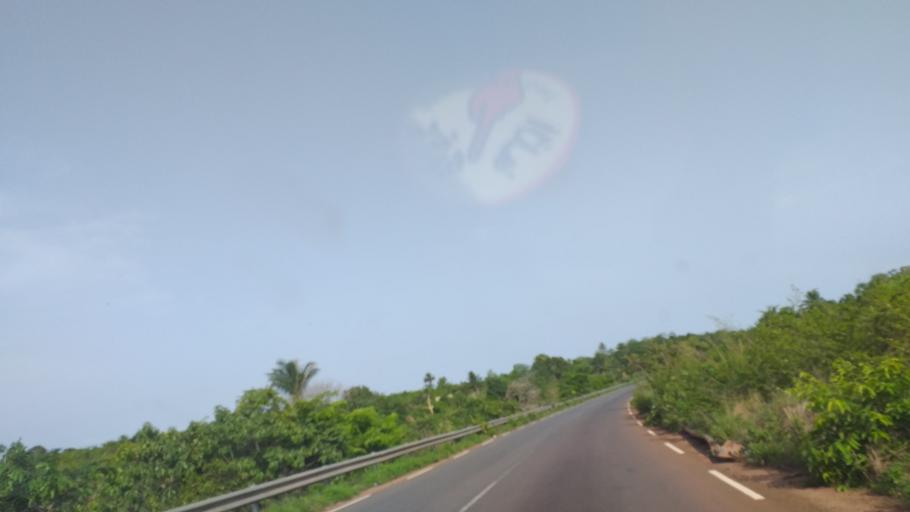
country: GN
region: Boke
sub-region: Boffa
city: Boffa
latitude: 10.2924
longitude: -14.1920
